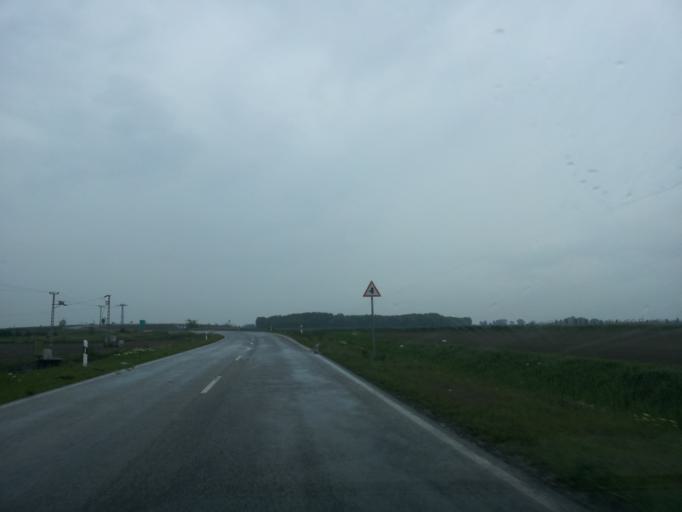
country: HU
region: Tolna
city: Ocseny
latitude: 46.3078
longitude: 18.7155
